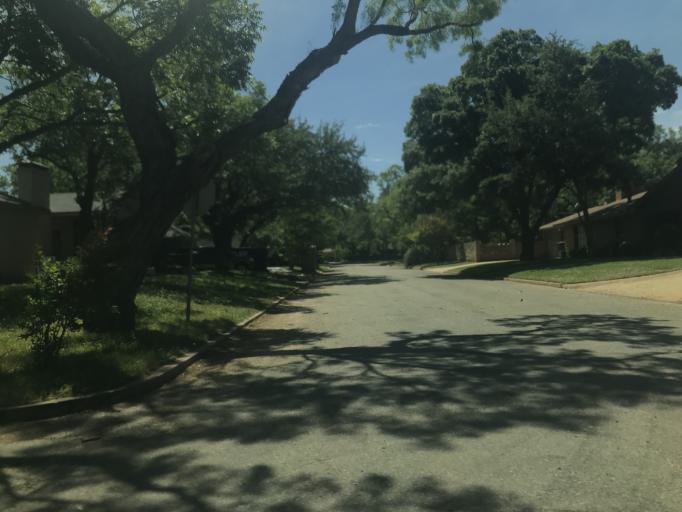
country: US
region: Texas
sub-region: Taylor County
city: Abilene
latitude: 32.4346
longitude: -99.7701
